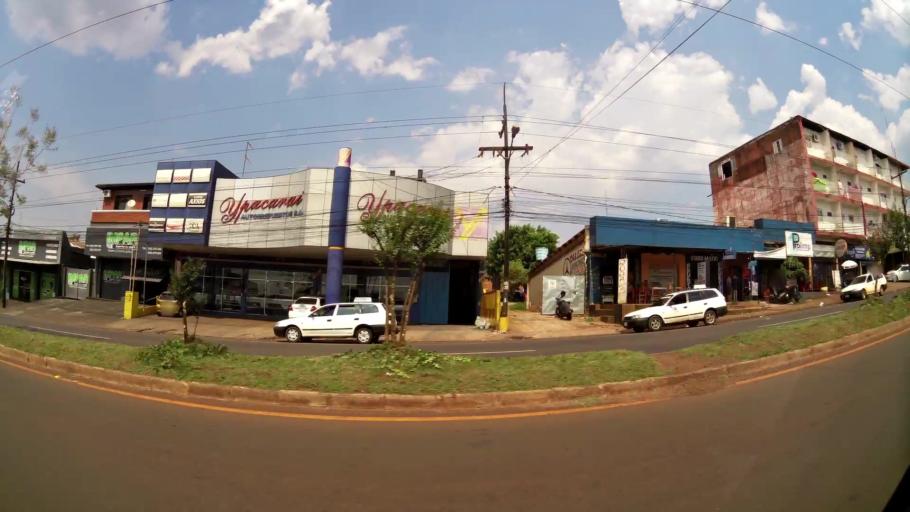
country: PY
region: Alto Parana
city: Ciudad del Este
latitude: -25.5053
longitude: -54.6380
